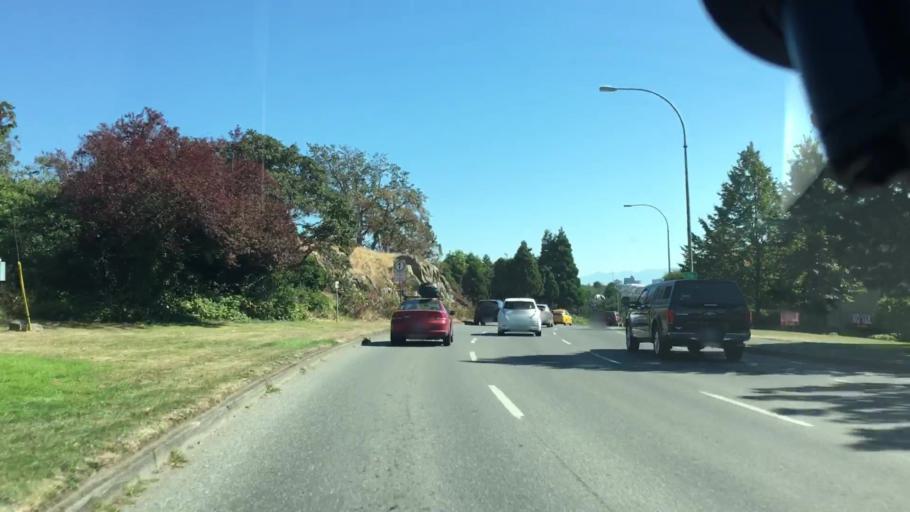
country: CA
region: British Columbia
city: Victoria
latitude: 48.4551
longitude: -123.3719
